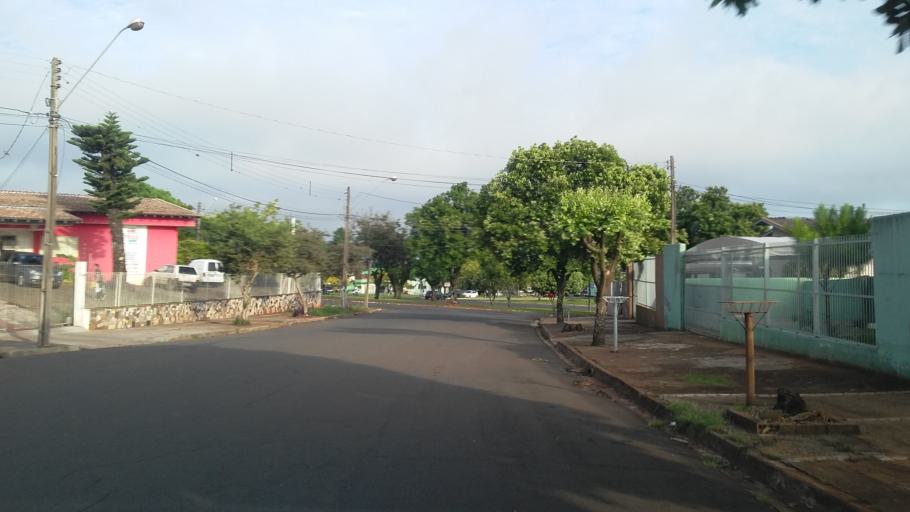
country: BR
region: Parana
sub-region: Londrina
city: Londrina
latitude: -23.2986
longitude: -51.1809
